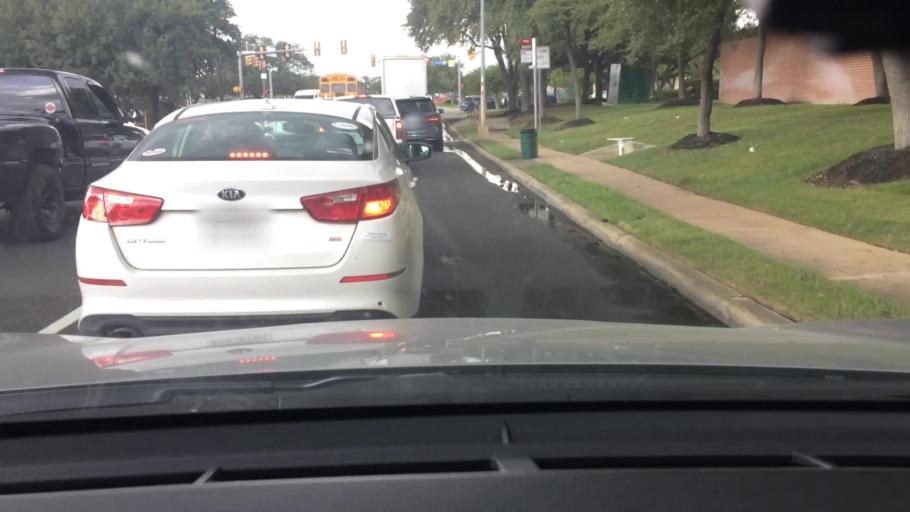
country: US
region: Texas
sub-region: Bexar County
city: Shavano Park
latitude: 29.5622
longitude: -98.5935
